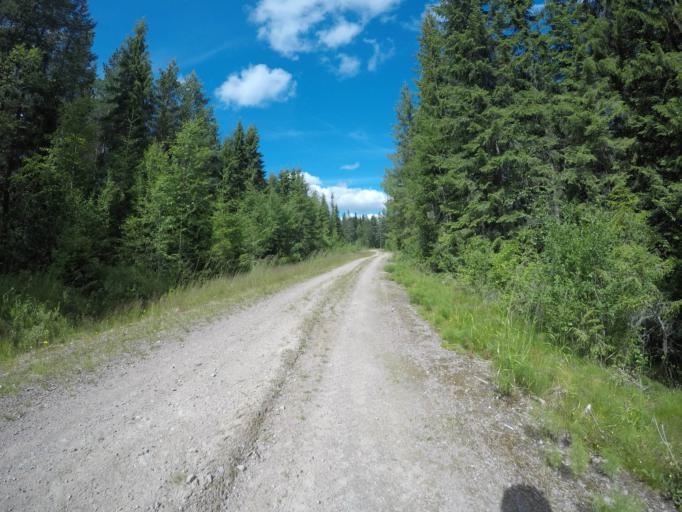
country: SE
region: Vaermland
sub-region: Filipstads Kommun
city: Lesjofors
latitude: 60.0757
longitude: 14.4586
